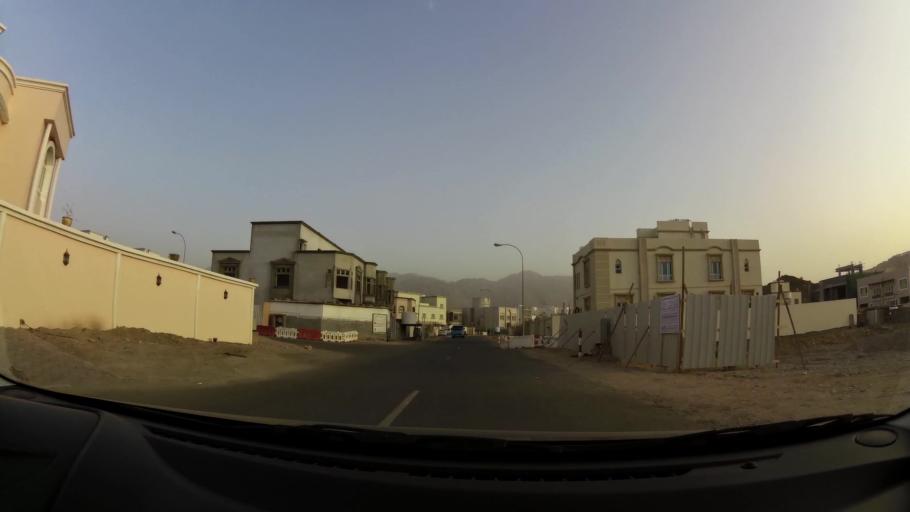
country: OM
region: Muhafazat Masqat
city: Bawshar
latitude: 23.4973
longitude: 58.3184
